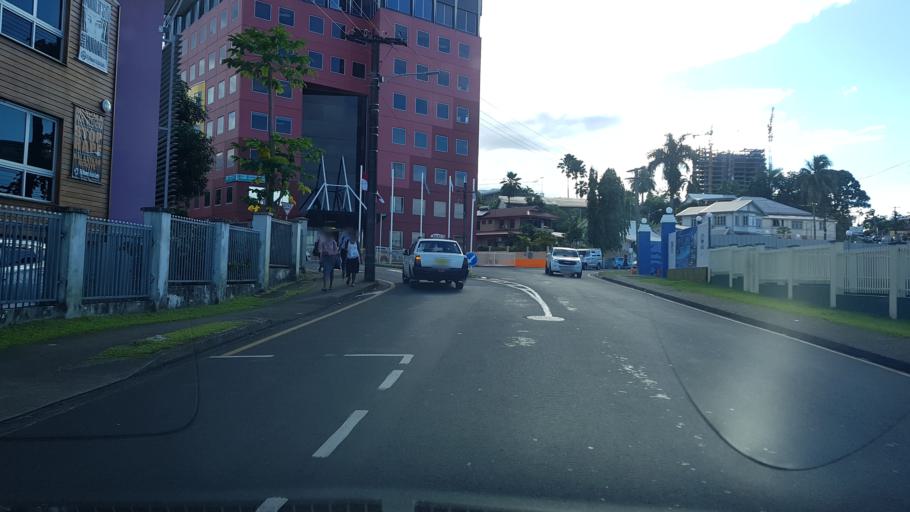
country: FJ
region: Central
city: Suva
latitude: -18.1444
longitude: 178.4258
